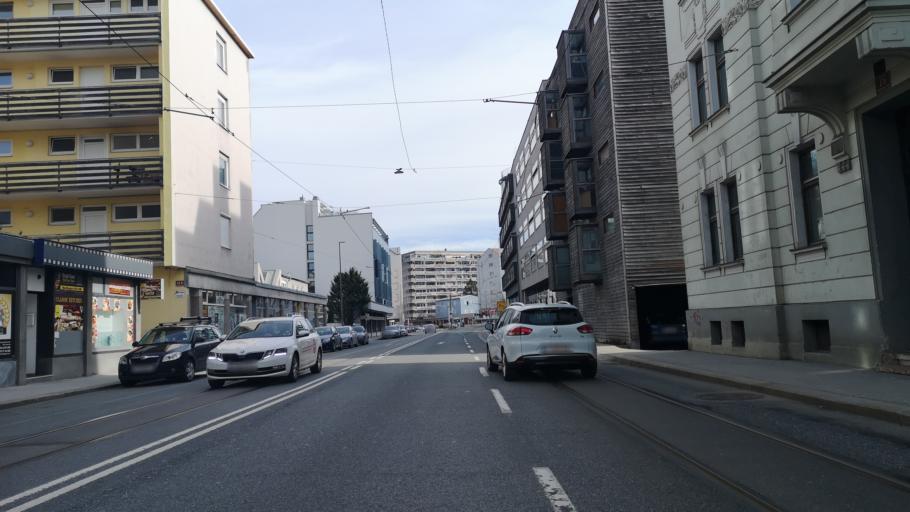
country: AT
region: Tyrol
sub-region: Innsbruck Stadt
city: Innsbruck
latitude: 47.2658
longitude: 11.3810
